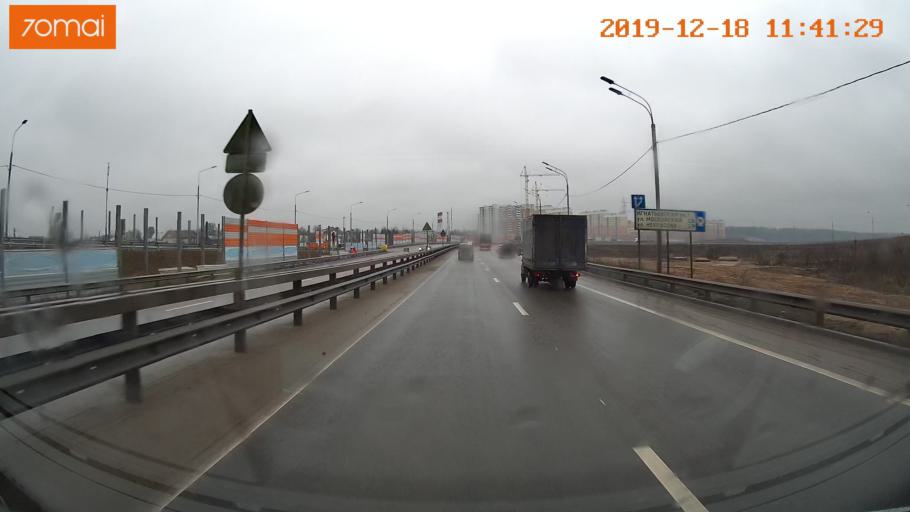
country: RU
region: Moskovskaya
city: Zvenigorod
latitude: 55.7139
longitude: 36.8722
